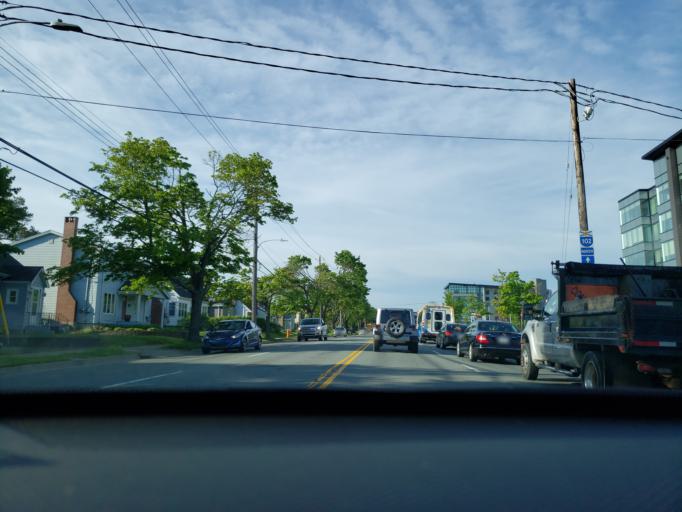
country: CA
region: Nova Scotia
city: Dartmouth
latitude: 44.6558
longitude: -63.6298
